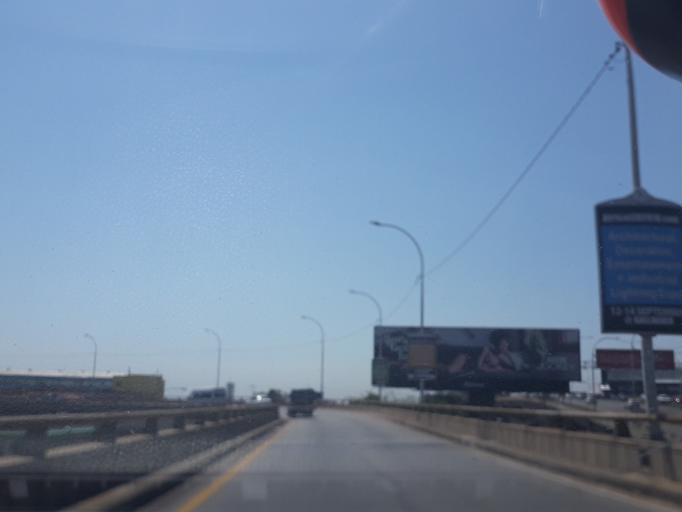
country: ZA
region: Gauteng
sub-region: City of Johannesburg Metropolitan Municipality
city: Johannesburg
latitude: -26.2122
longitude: 28.0410
